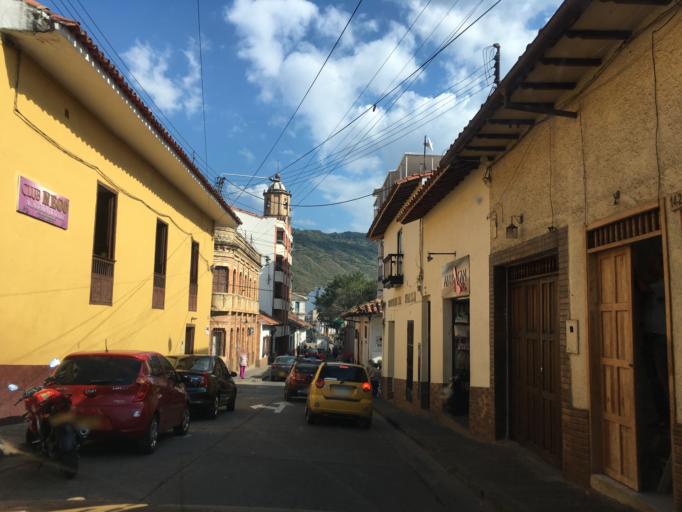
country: CO
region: Santander
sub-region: San Gil
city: San Gil
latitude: 6.5561
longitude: -73.1347
